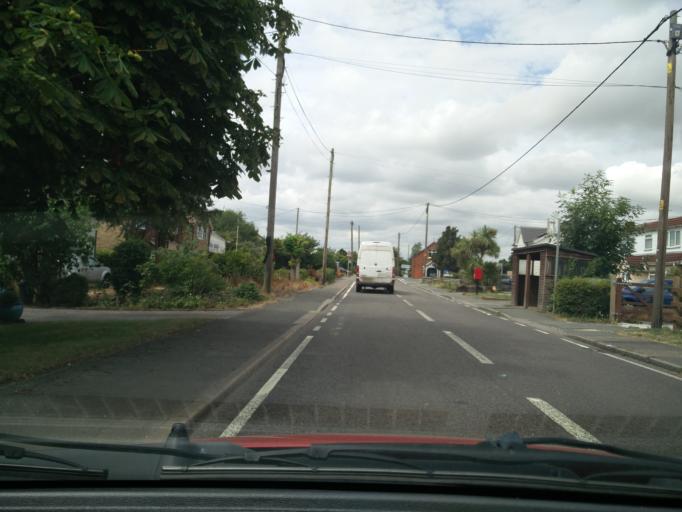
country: GB
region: England
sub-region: Essex
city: Burnham on Crouch
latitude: 51.6555
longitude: 0.7626
